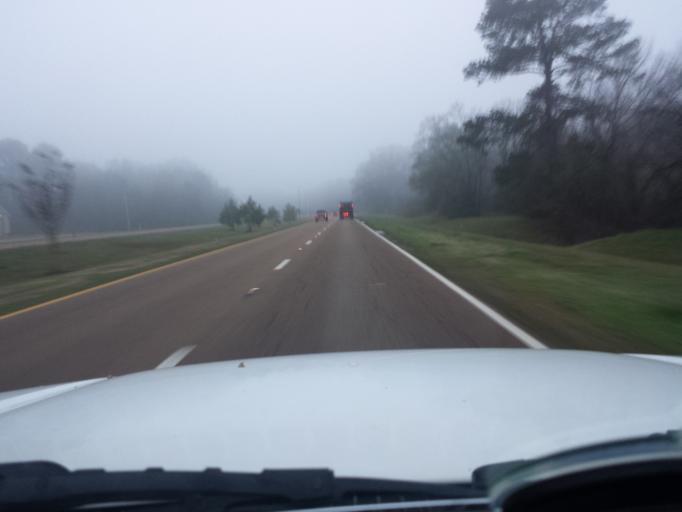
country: US
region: Mississippi
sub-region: Rankin County
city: Flowood
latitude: 32.2895
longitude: -90.1522
